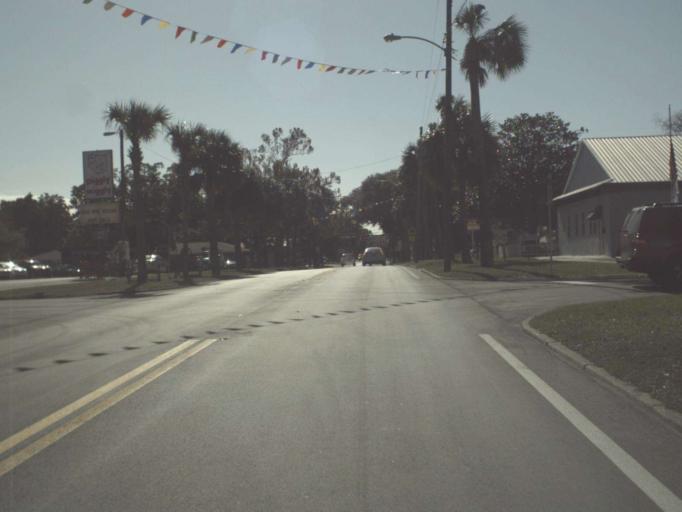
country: US
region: Florida
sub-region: Franklin County
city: Apalachicola
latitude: 29.7234
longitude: -84.9892
